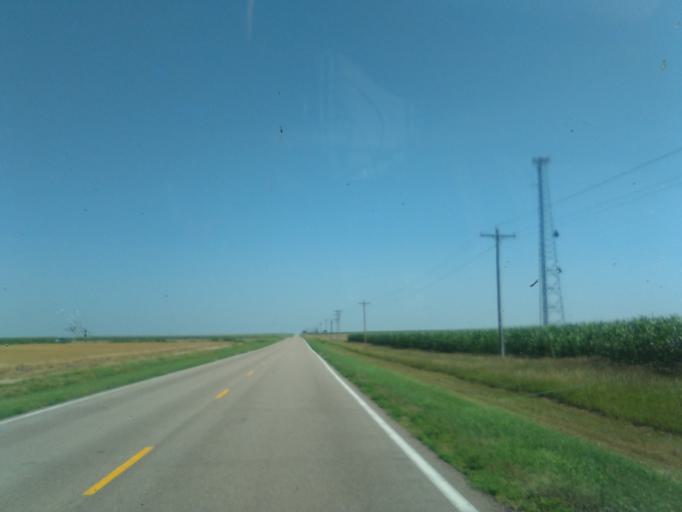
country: US
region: Kansas
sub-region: Cheyenne County
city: Saint Francis
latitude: 39.7766
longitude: -101.5420
